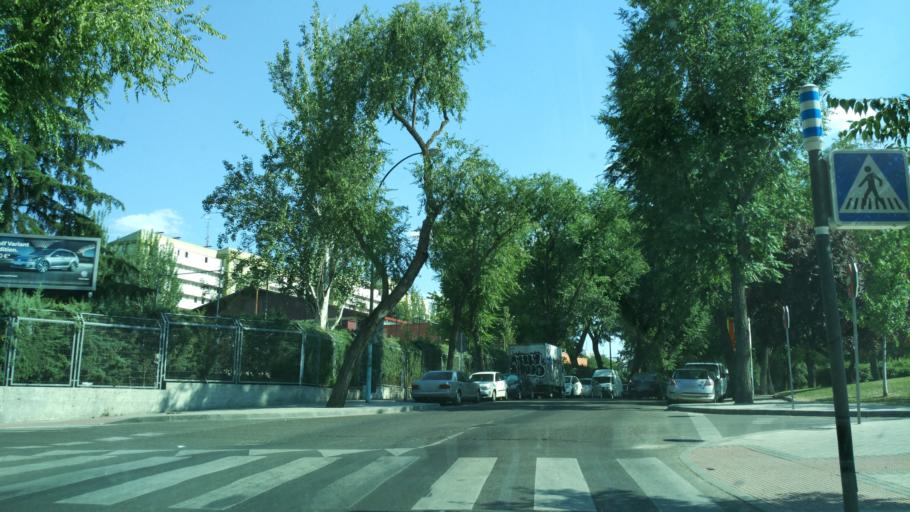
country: ES
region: Madrid
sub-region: Provincia de Madrid
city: Tetuan de las Victorias
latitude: 40.4621
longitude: -3.7123
